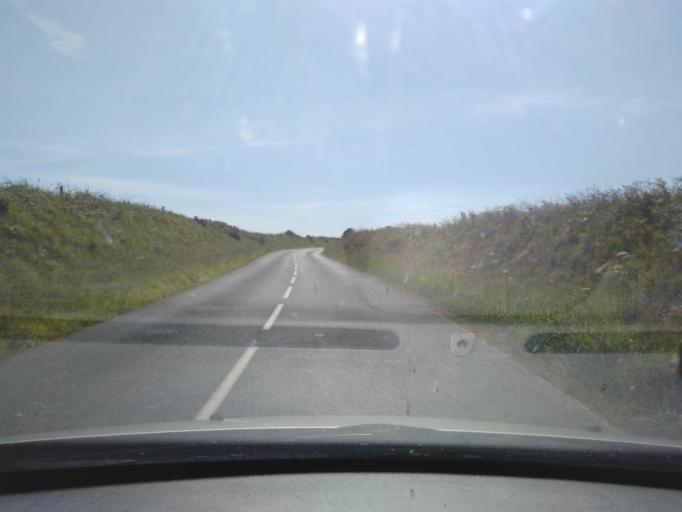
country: FR
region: Lower Normandy
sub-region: Departement de la Manche
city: Beaumont-Hague
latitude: 49.6973
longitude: -1.9247
